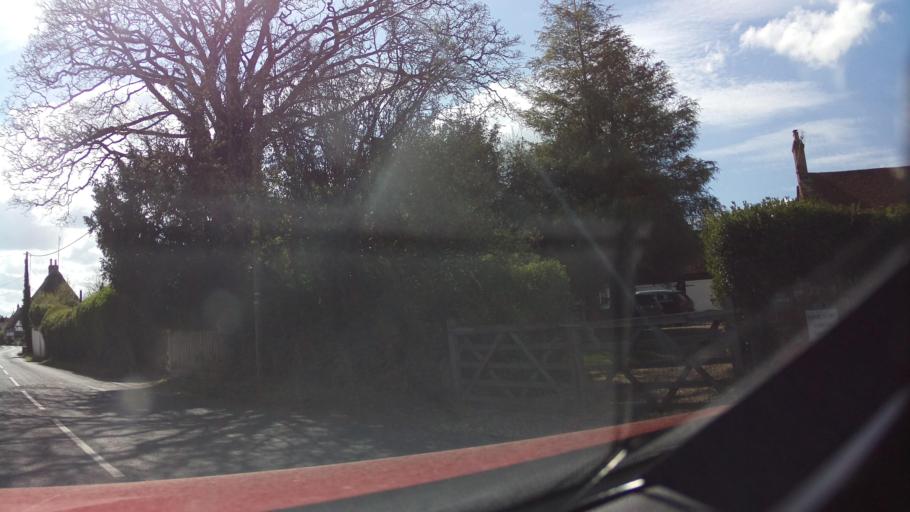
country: GB
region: England
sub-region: Hampshire
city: Andover
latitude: 51.1777
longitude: -1.4840
